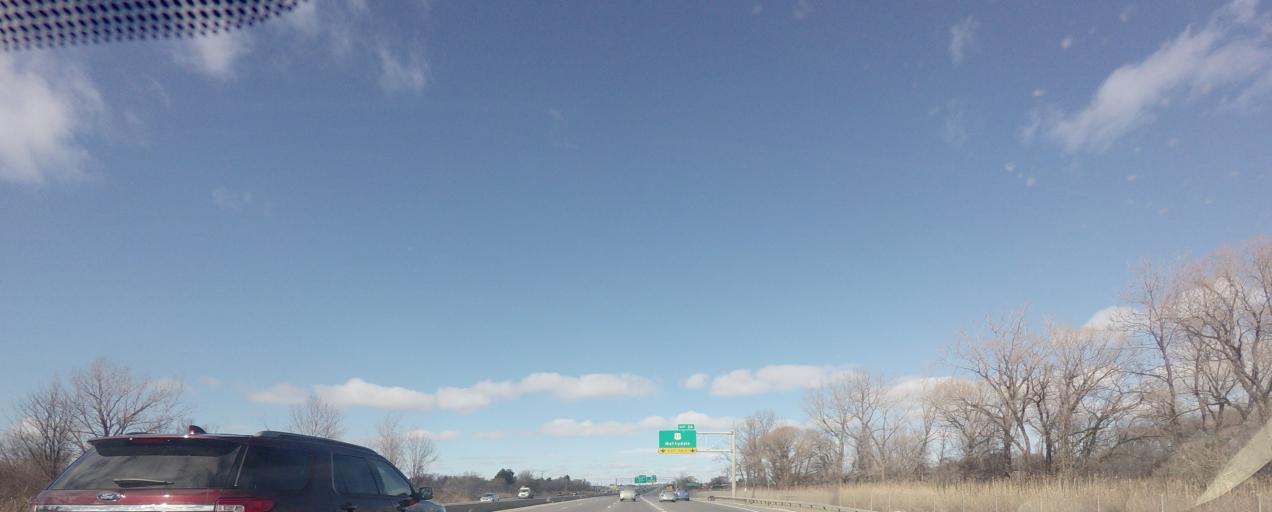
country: US
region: New York
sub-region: Onondaga County
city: Mattydale
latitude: 43.1047
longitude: -76.1525
